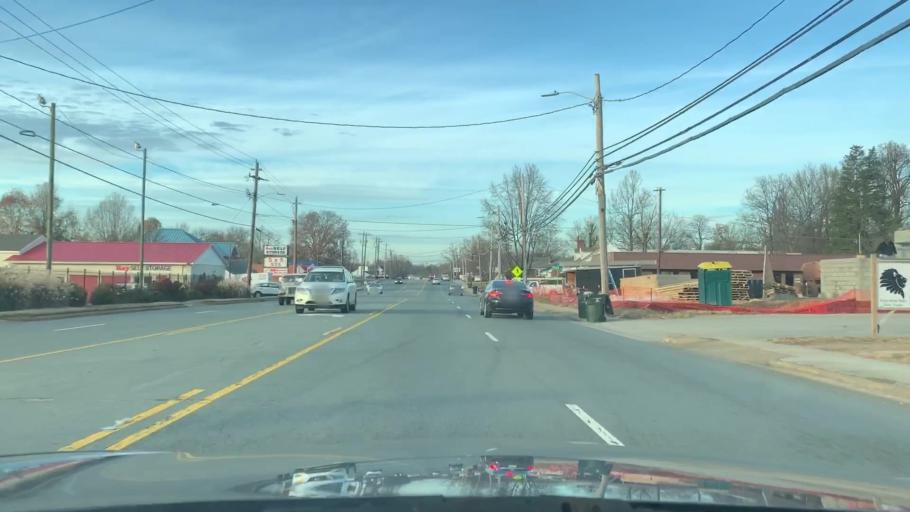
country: US
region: North Carolina
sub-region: Alamance County
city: Burlington
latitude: 36.0713
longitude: -79.4277
